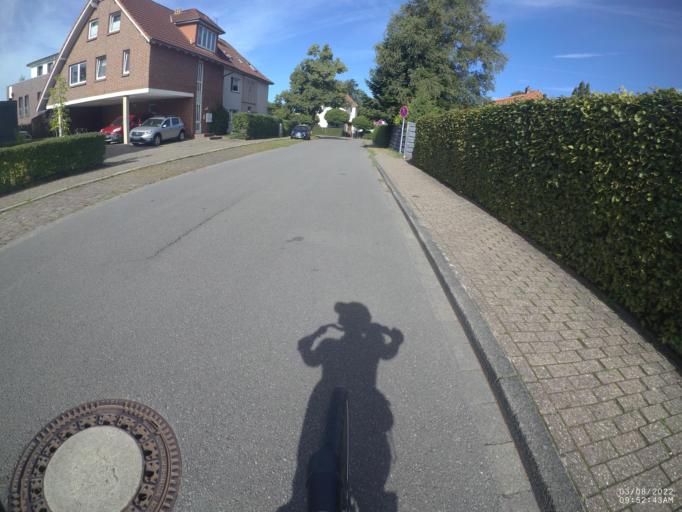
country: DE
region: Lower Saxony
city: Oldenburg
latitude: 53.1435
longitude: 8.1855
